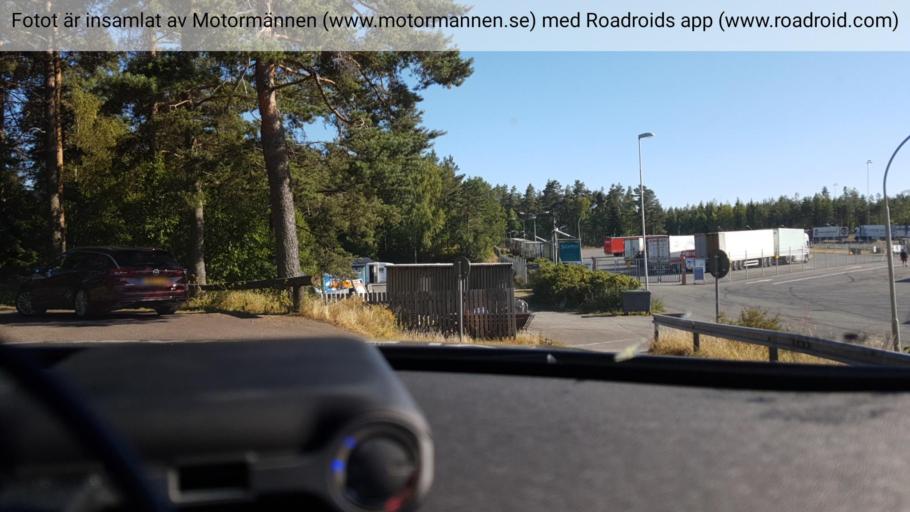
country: SE
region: Joenkoeping
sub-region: Jonkopings Kommun
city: Odensjo
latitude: 57.6664
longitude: 14.1824
